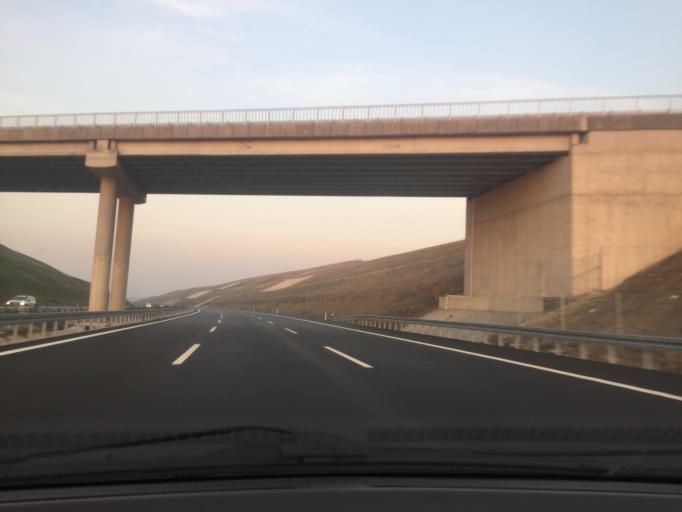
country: TR
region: Bursa
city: Mahmudiye
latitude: 40.2771
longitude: 28.5422
